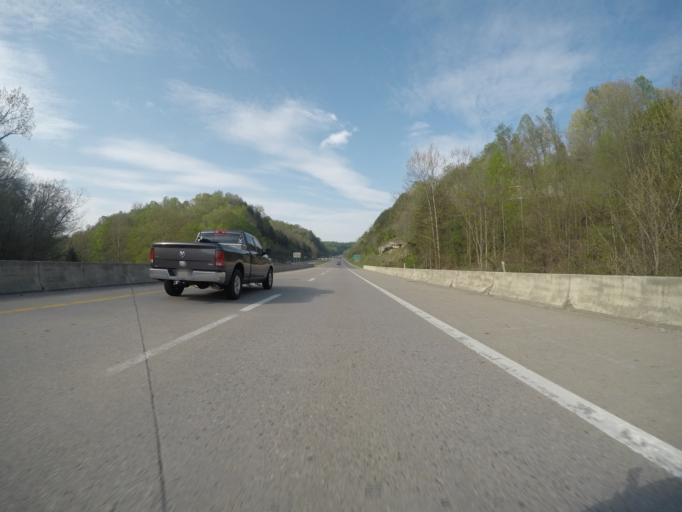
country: US
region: West Virginia
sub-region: Kanawha County
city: Dunbar
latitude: 38.3121
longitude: -81.7286
